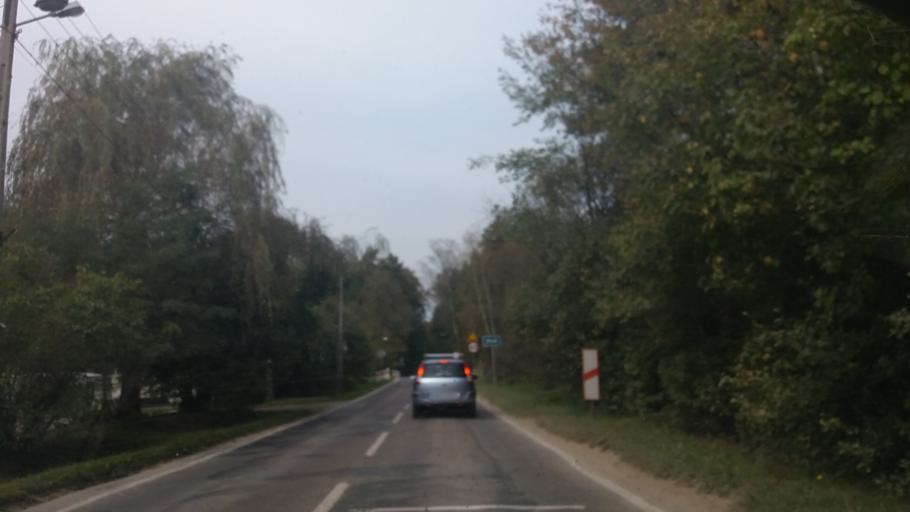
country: PL
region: Lesser Poland Voivodeship
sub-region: Powiat chrzanowski
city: Pogorzyce
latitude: 50.1130
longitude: 19.4426
